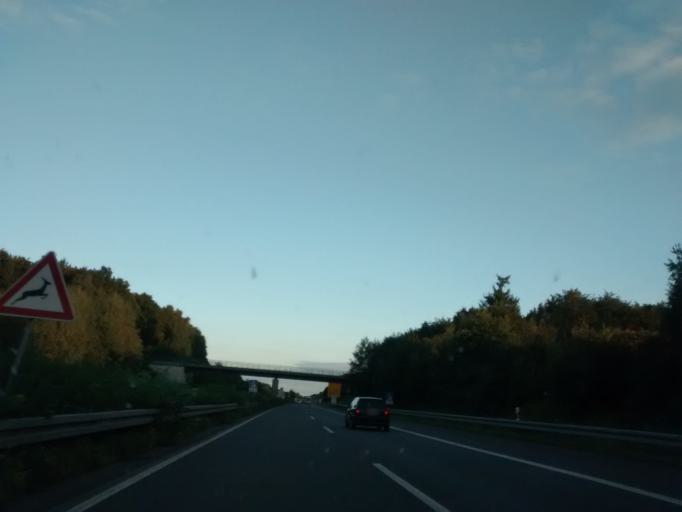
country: DE
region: Lower Saxony
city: Dissen
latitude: 52.0861
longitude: 8.2336
